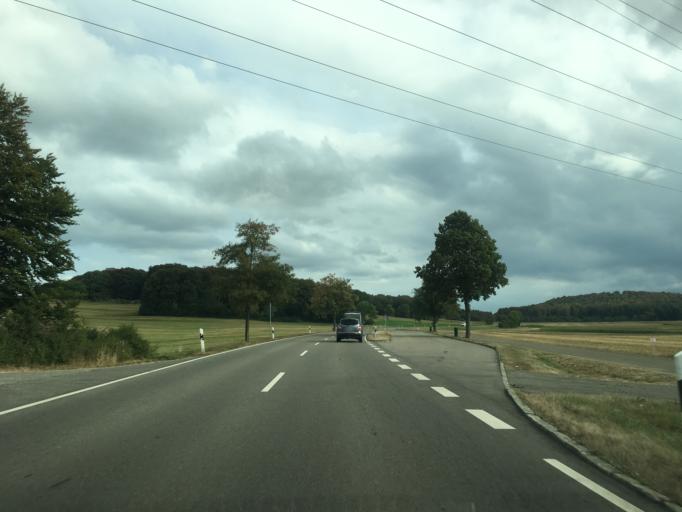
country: DE
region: Baden-Wuerttemberg
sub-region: Tuebingen Region
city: Sankt Johann
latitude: 48.3814
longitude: 9.3099
